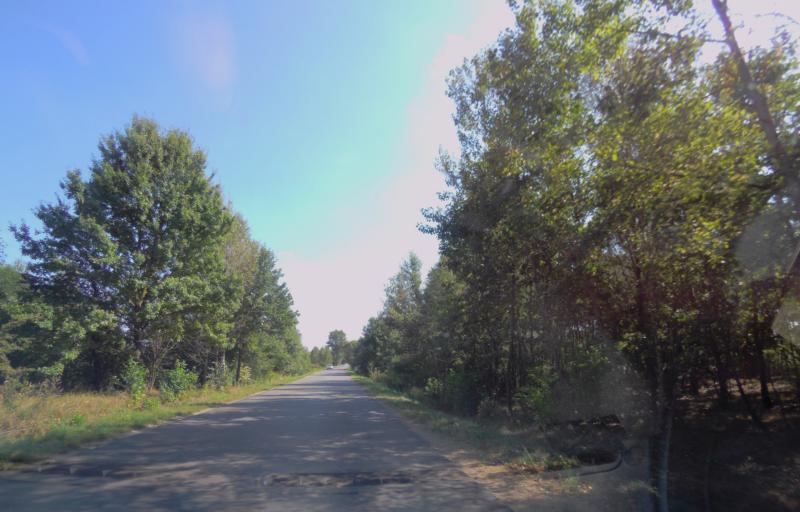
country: PL
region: Subcarpathian Voivodeship
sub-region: Powiat lezajski
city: Wola Zarczycka
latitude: 50.2825
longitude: 22.2861
